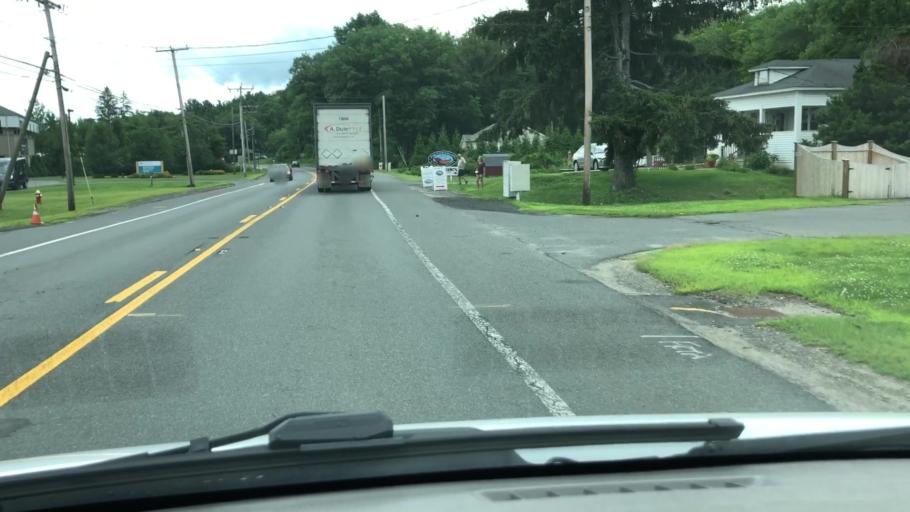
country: US
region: Massachusetts
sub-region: Hampshire County
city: Hatfield
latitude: 42.3674
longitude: -72.6375
